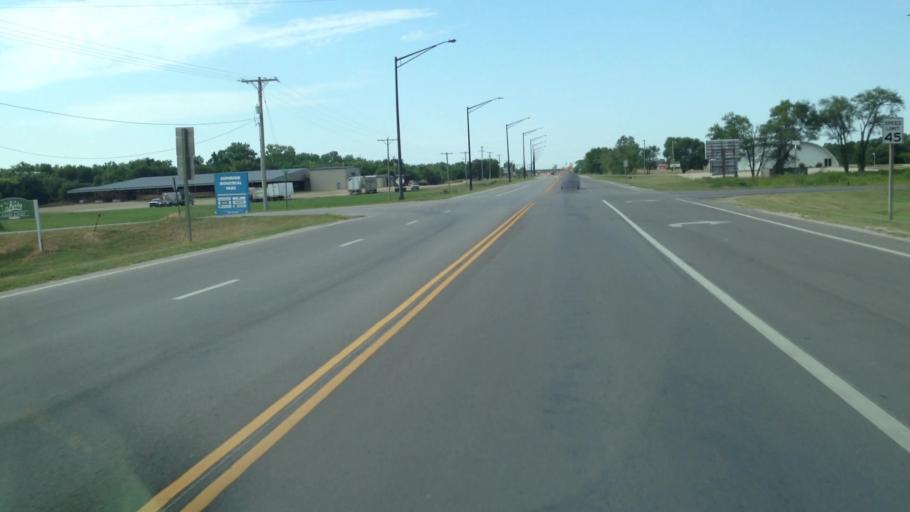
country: US
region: Kansas
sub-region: Labette County
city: Parsons
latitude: 37.3546
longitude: -95.2589
